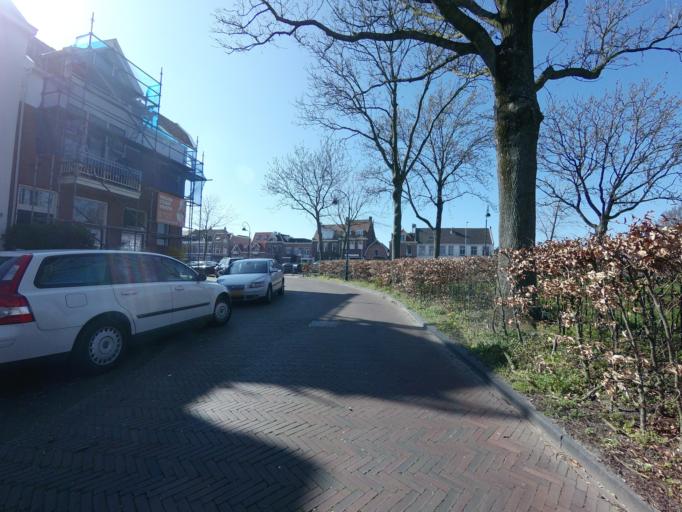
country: NL
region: North Holland
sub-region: Gemeente Haarlem
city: Haarlem
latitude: 52.3709
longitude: 4.6190
